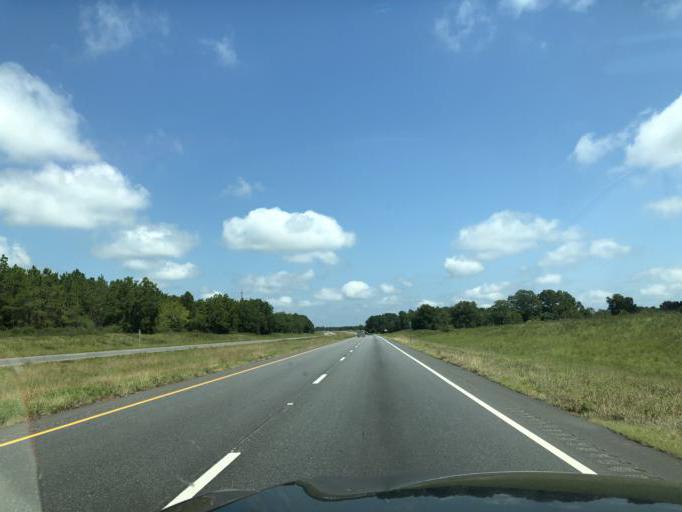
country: US
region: Alabama
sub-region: Henry County
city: Abbeville
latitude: 31.4975
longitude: -85.2939
